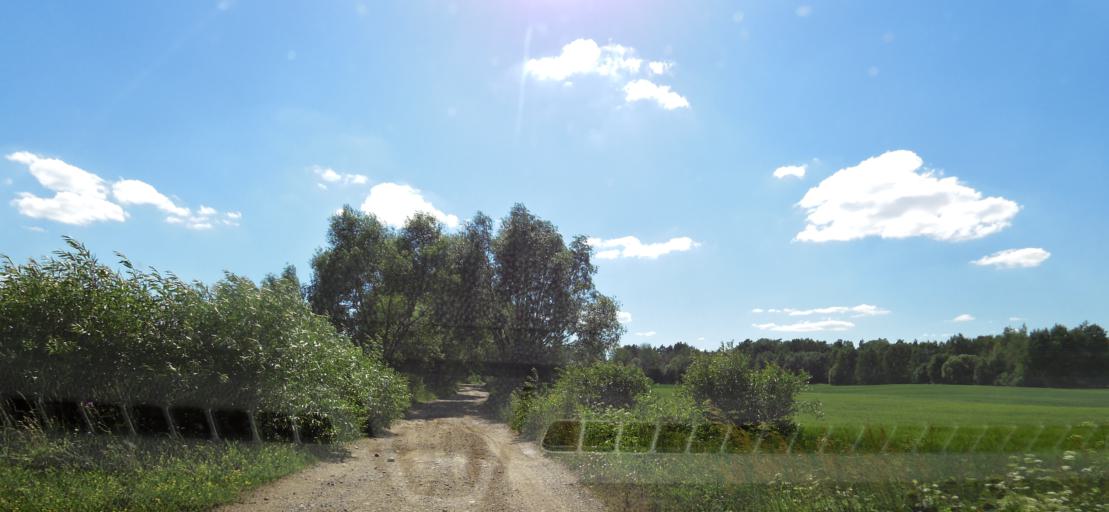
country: LT
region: Vilnius County
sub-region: Vilnius
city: Fabijoniskes
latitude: 54.8421
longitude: 25.3318
